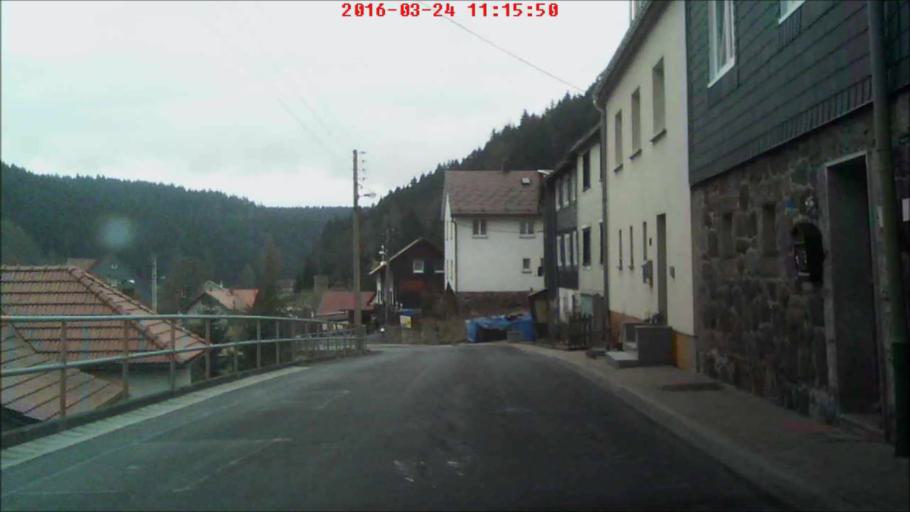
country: DE
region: Thuringia
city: Masserberg
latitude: 50.5049
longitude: 10.9437
